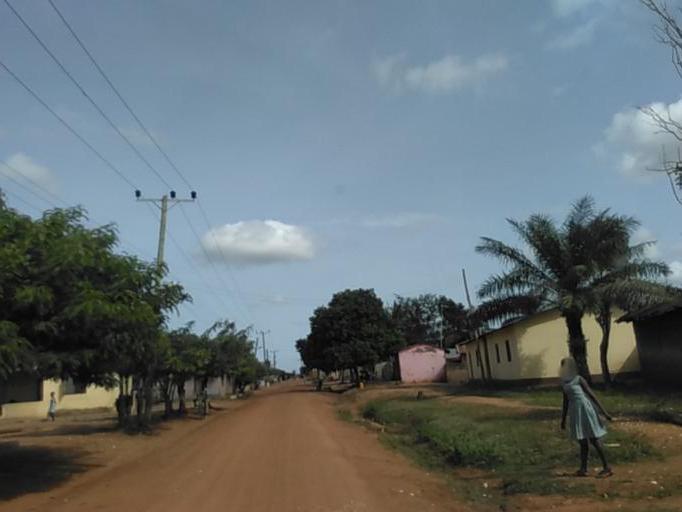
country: GH
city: Akropong
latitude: 6.0318
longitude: 0.3746
